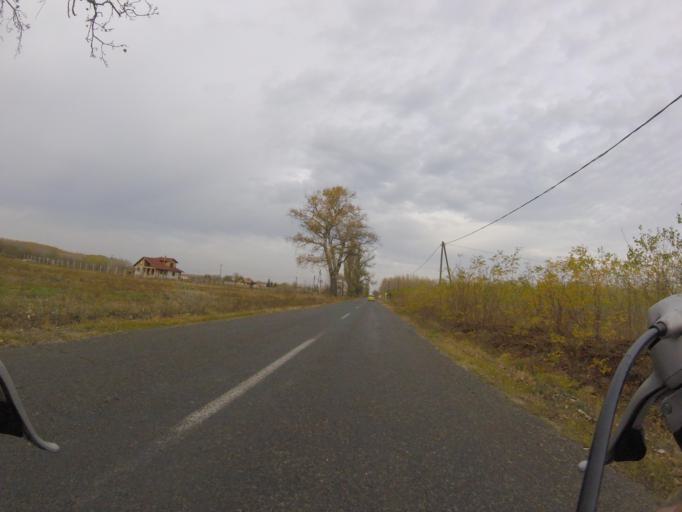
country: HU
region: Pest
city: Csemo
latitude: 47.1066
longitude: 19.6886
